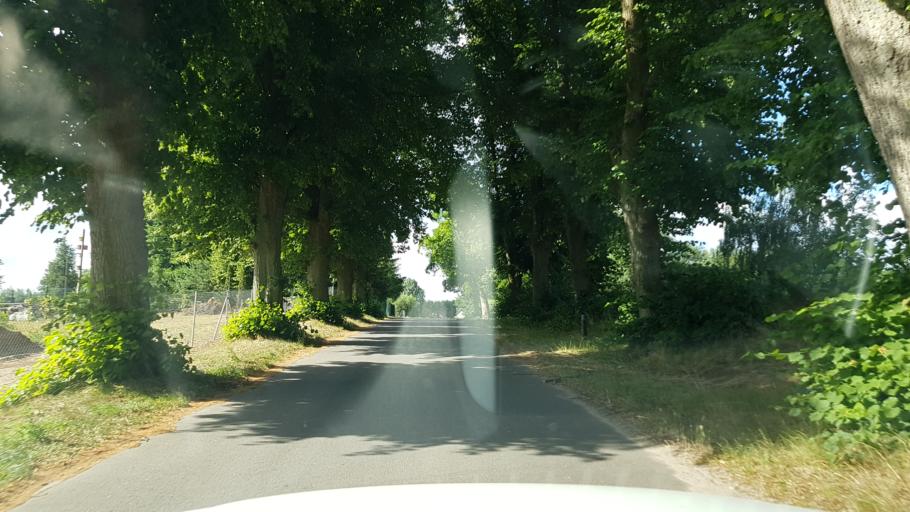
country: PL
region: West Pomeranian Voivodeship
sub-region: Powiat mysliborski
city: Debno
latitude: 52.7311
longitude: 14.6651
